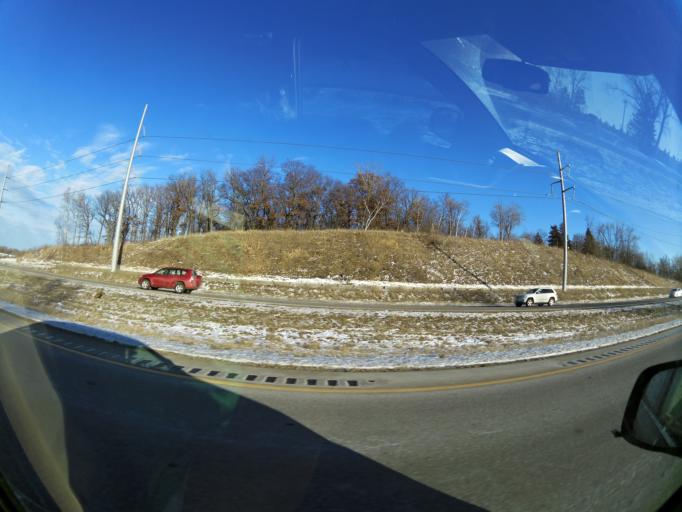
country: US
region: Minnesota
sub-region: Dakota County
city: Inver Grove Heights
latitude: 44.7930
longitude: -93.0371
